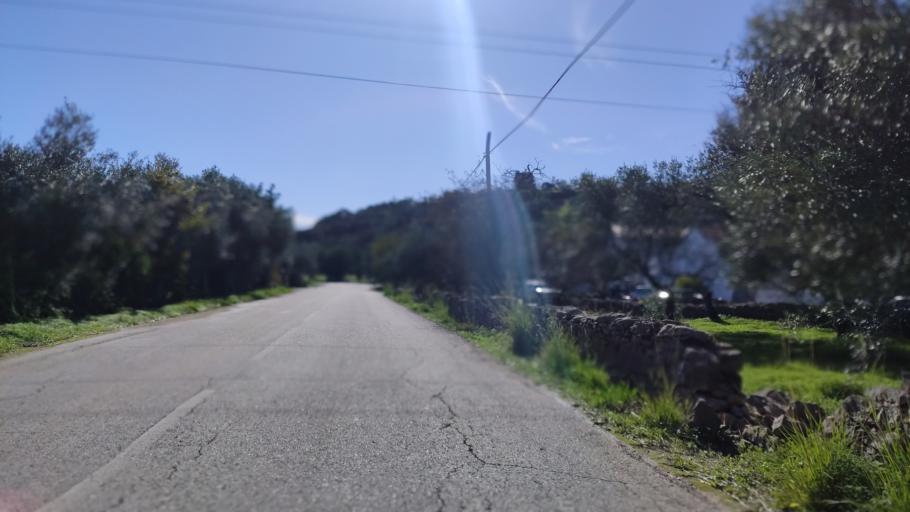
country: PT
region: Faro
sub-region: Sao Bras de Alportel
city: Sao Bras de Alportel
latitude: 37.1539
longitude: -7.8561
